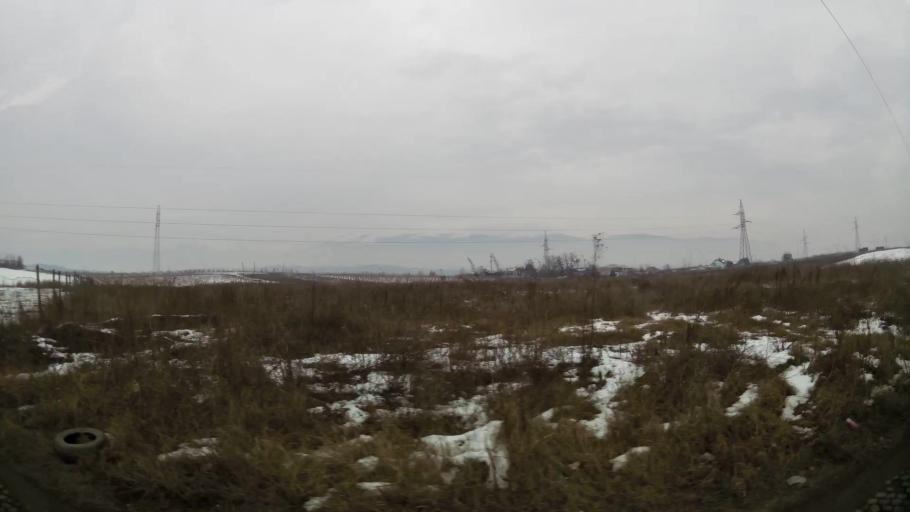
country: MK
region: Suto Orizari
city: Suto Orizare
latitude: 42.0455
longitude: 21.4327
